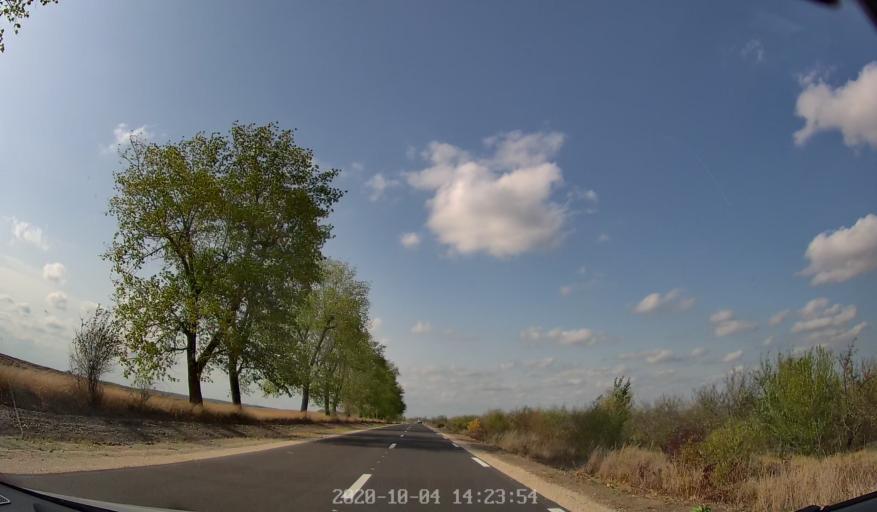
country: MD
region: Rezina
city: Saharna
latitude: 47.6116
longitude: 28.9276
